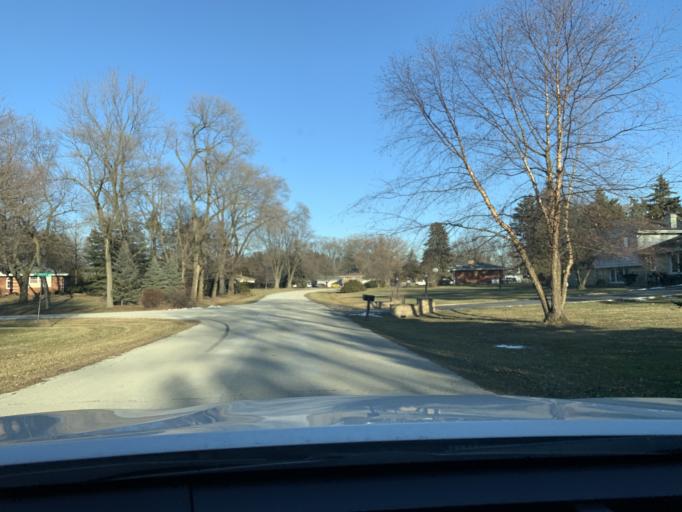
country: US
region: Illinois
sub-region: Cook County
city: Lemont
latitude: 41.7114
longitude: -88.0133
